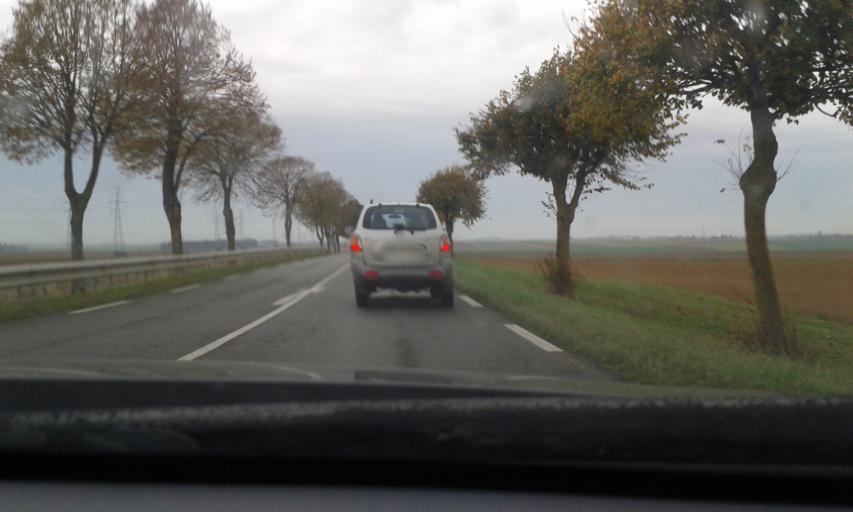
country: FR
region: Centre
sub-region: Departement d'Eure-et-Loir
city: Baigneaux
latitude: 48.1504
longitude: 1.8448
